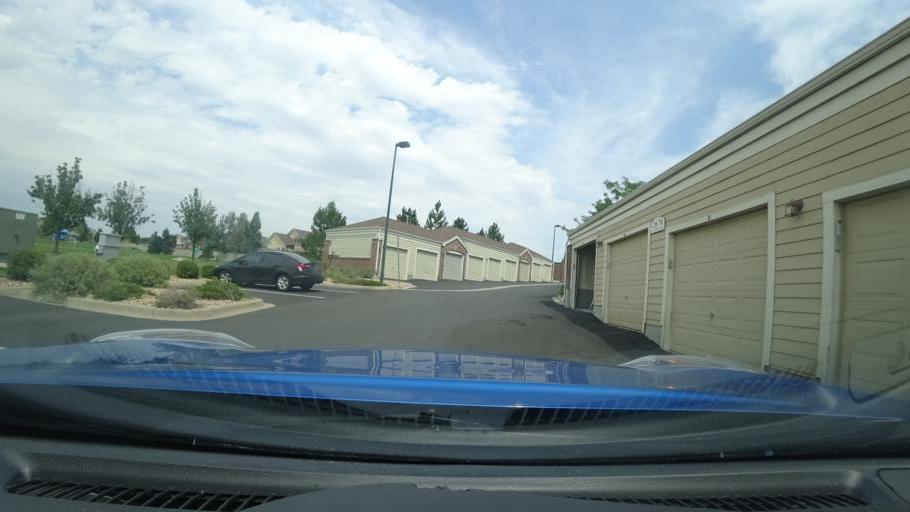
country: US
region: Colorado
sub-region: Adams County
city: Aurora
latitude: 39.6692
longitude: -104.7650
